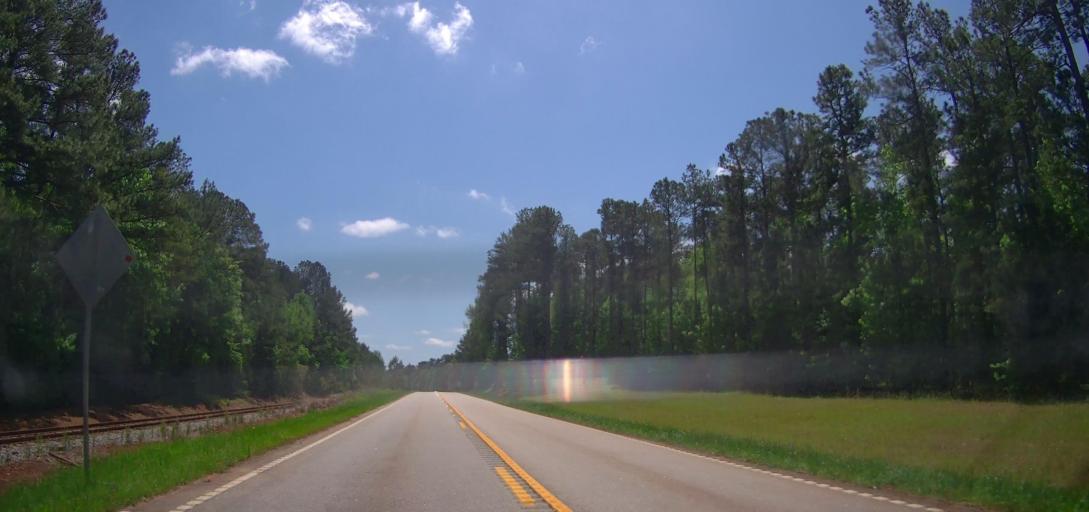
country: US
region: Georgia
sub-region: Jasper County
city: Monticello
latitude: 33.1602
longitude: -83.6413
